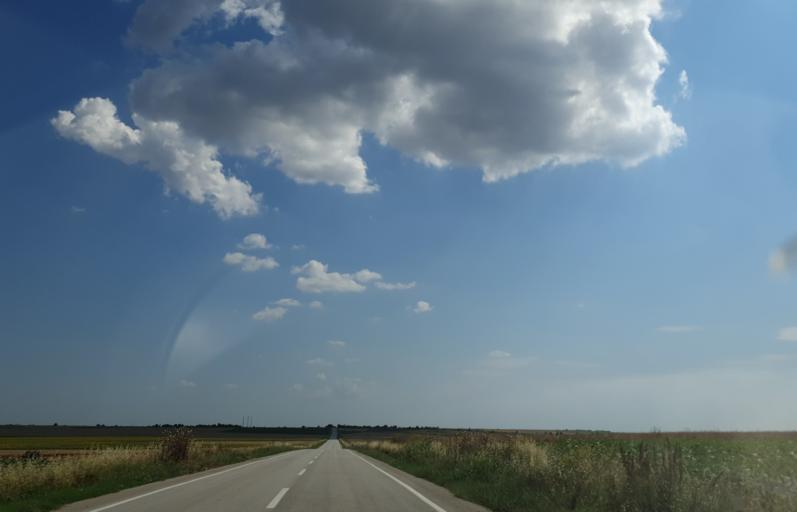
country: TR
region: Kirklareli
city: Buyukkaristiran
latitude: 41.3954
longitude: 27.5730
